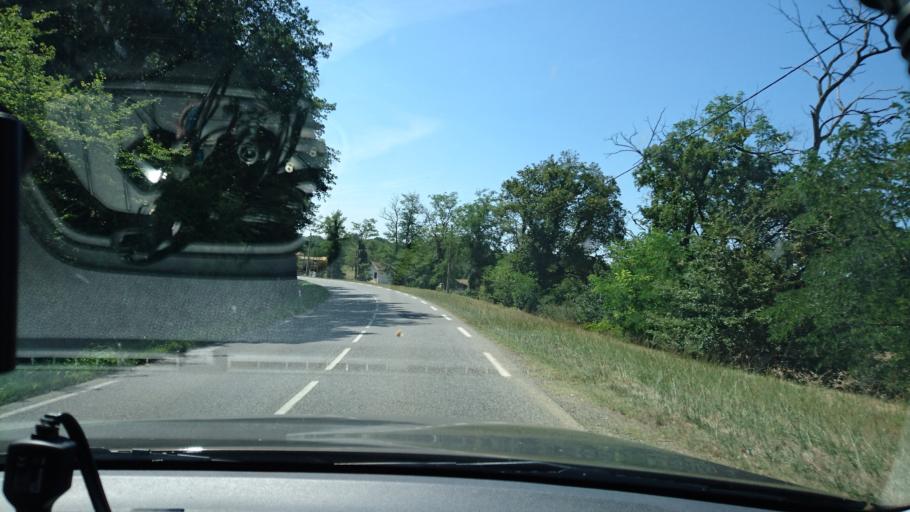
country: FR
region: Midi-Pyrenees
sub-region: Departement de la Haute-Garonne
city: Noe
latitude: 43.3404
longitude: 1.2702
